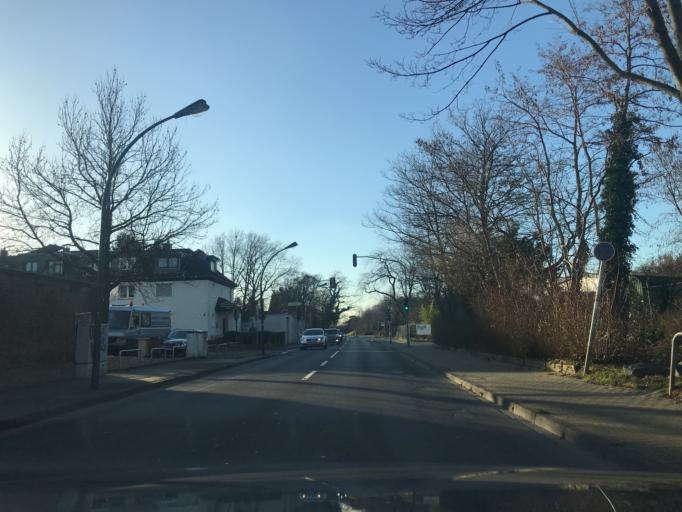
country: DE
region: North Rhine-Westphalia
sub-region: Regierungsbezirk Dusseldorf
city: Dusseldorf
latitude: 51.2712
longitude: 6.7689
